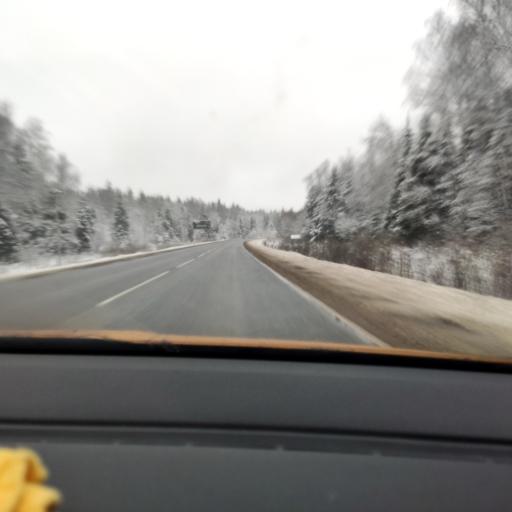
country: RU
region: Moskovskaya
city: Yershovo
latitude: 55.8007
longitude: 36.9414
